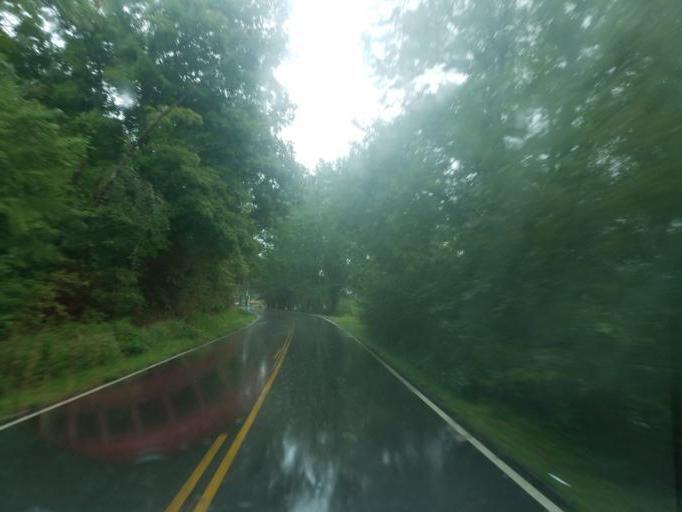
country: US
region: Kentucky
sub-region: Greenup County
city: Greenup
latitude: 38.4990
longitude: -82.9706
